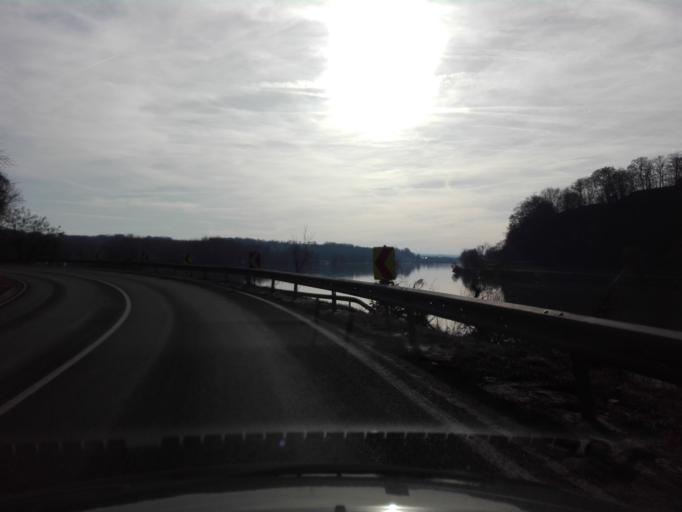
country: AT
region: Lower Austria
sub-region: Politischer Bezirk Amstetten
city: Amstetten
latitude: 48.1989
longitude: 14.8479
